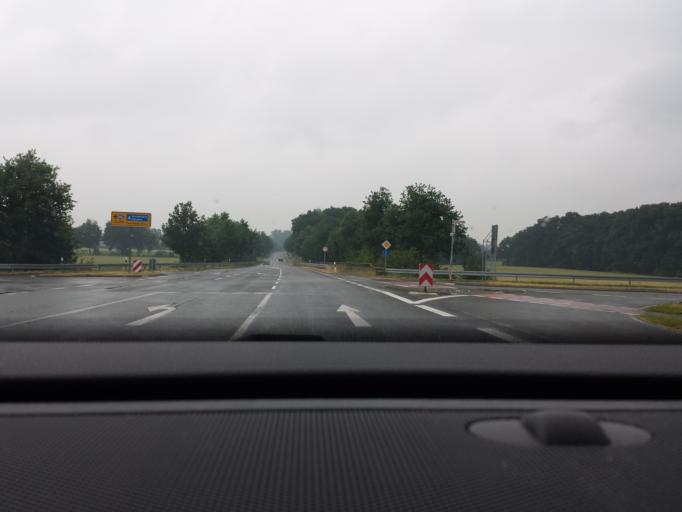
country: DE
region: North Rhine-Westphalia
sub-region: Regierungsbezirk Munster
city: Gronau
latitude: 52.1921
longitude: 6.9752
